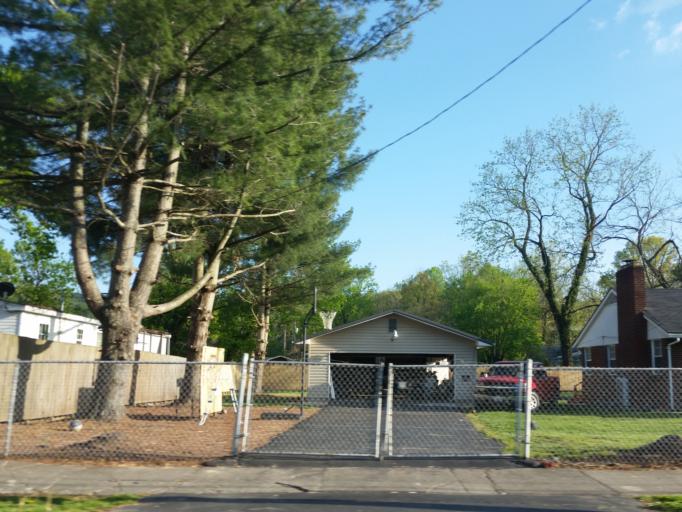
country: US
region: Kentucky
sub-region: Bell County
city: Middlesboro
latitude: 36.6033
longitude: -83.7206
